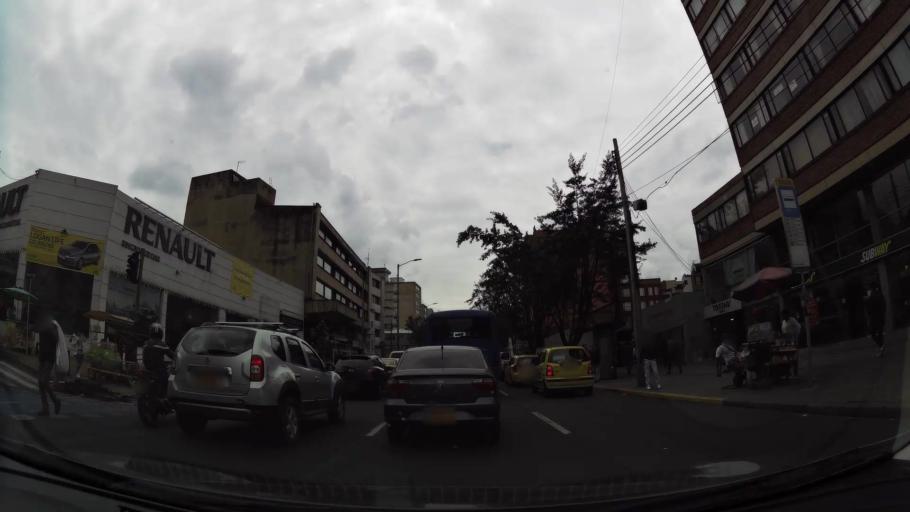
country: CO
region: Bogota D.C.
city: Bogota
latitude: 4.6342
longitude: -74.0661
